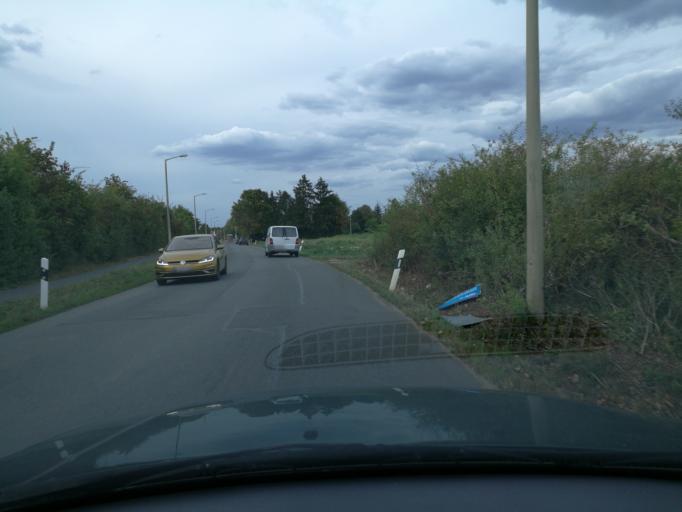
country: DE
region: Bavaria
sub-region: Regierungsbezirk Mittelfranken
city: Wetzendorf
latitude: 49.5041
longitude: 11.0463
